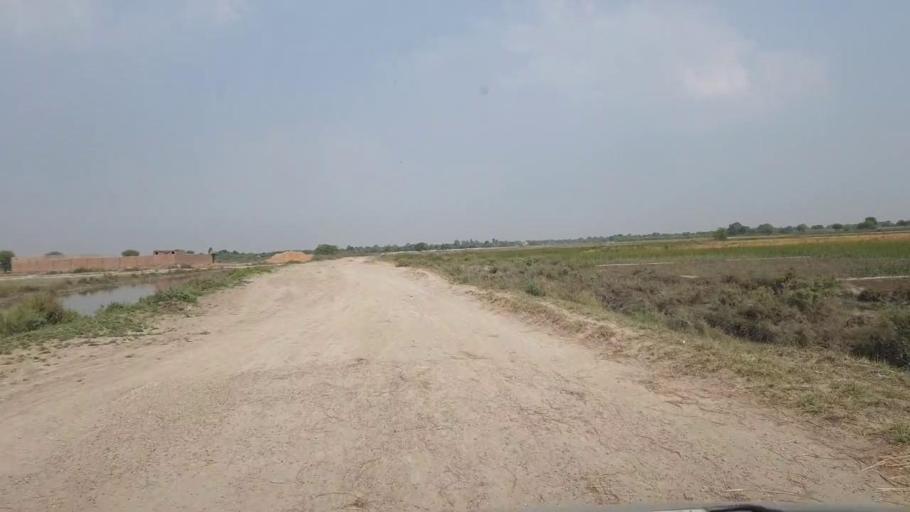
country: PK
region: Sindh
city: Matli
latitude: 24.9682
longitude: 68.6936
